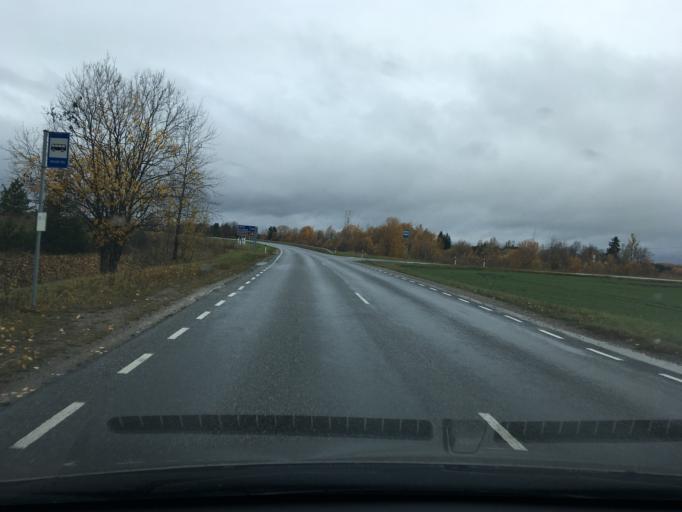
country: EE
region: Jogevamaa
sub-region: Tabivere vald
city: Tabivere
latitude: 58.4687
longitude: 26.6203
